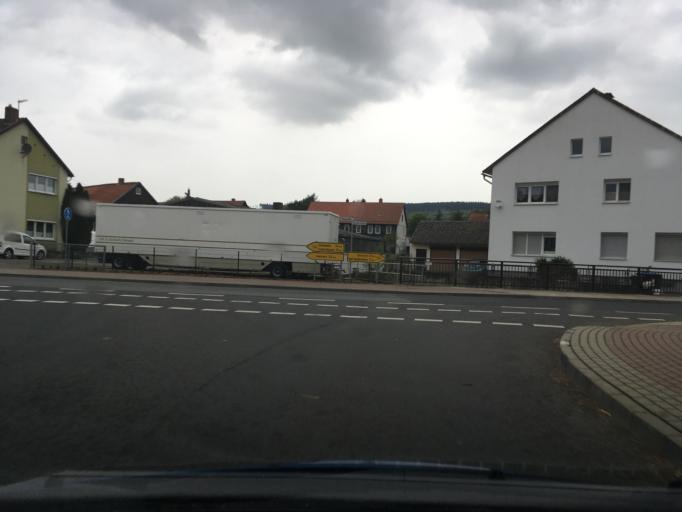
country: DE
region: Lower Saxony
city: Eimen
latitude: 51.8696
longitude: 9.8112
